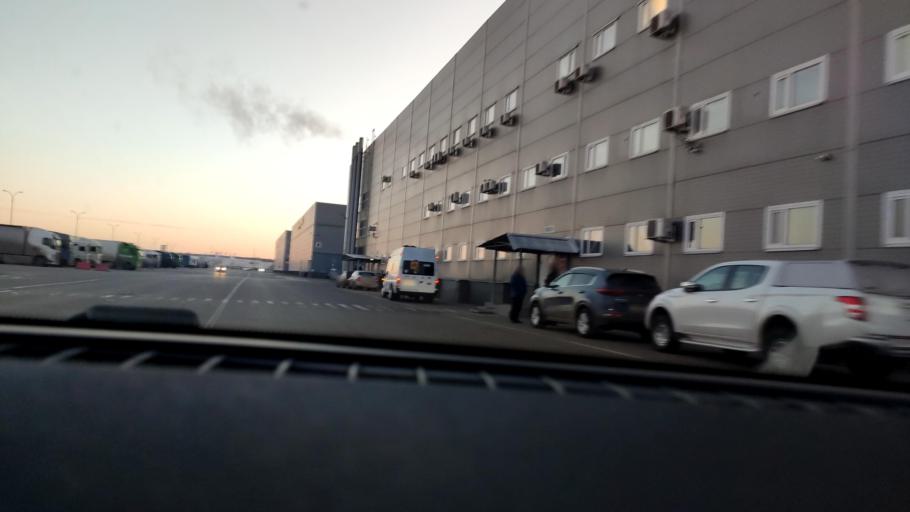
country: RU
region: Samara
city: Samara
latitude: 53.0972
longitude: 50.1335
